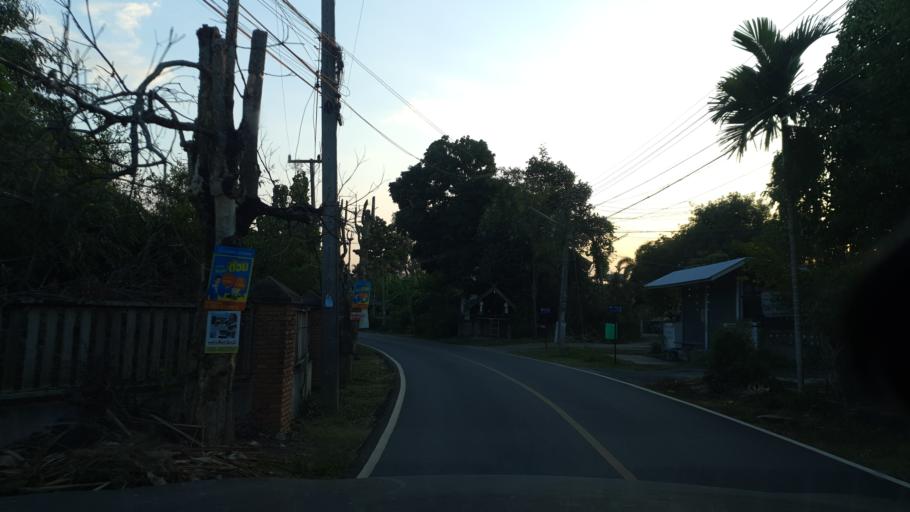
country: TH
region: Chiang Mai
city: San Sai
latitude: 18.8538
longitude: 99.0734
